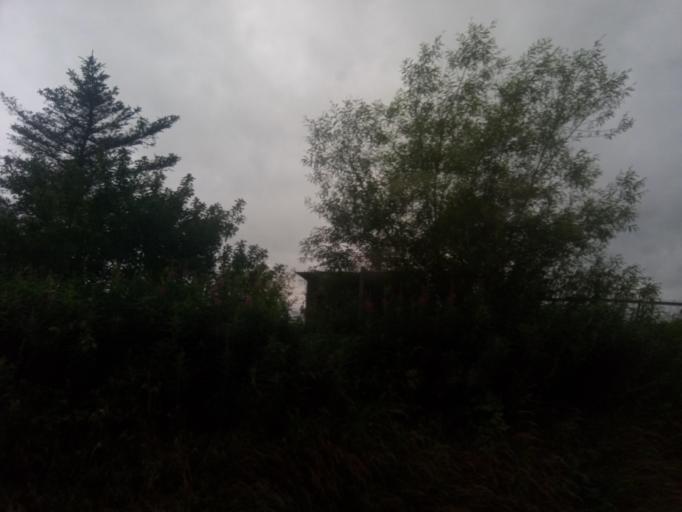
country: GB
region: England
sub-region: North Yorkshire
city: Settle
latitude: 54.0196
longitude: -2.2598
